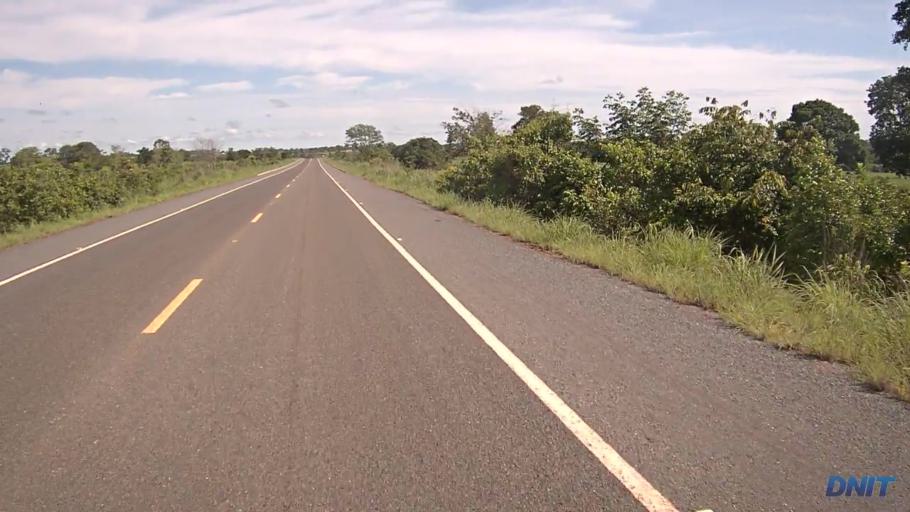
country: BR
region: Goias
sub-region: Sao Miguel Do Araguaia
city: Sao Miguel do Araguaia
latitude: -13.3086
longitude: -50.1723
